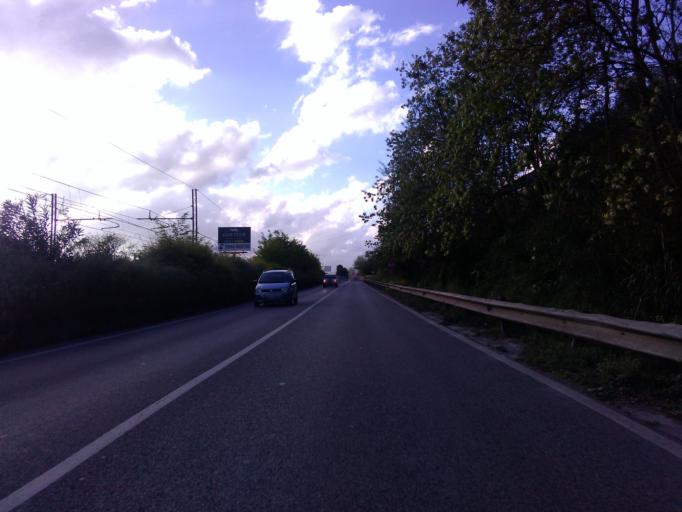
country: IT
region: Tuscany
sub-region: Provincia di Massa-Carrara
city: Capanne-Prato-Cinquale
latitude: 44.0017
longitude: 10.1668
